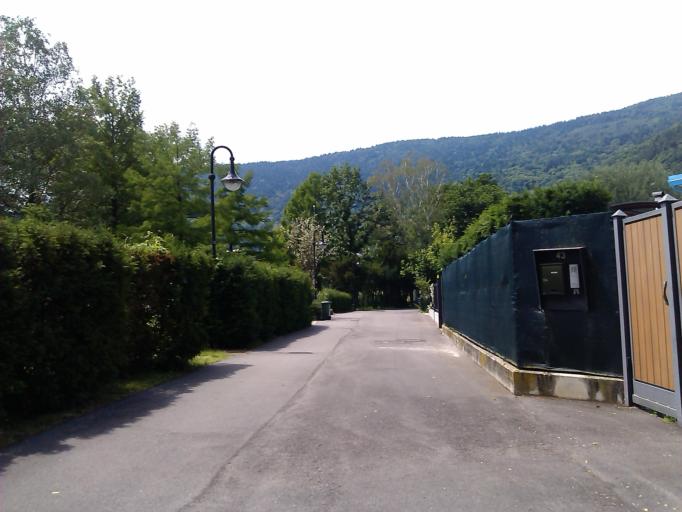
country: IT
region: Trentino-Alto Adige
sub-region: Provincia di Trento
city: Pergine Valsugana
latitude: 46.0372
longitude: 11.2371
